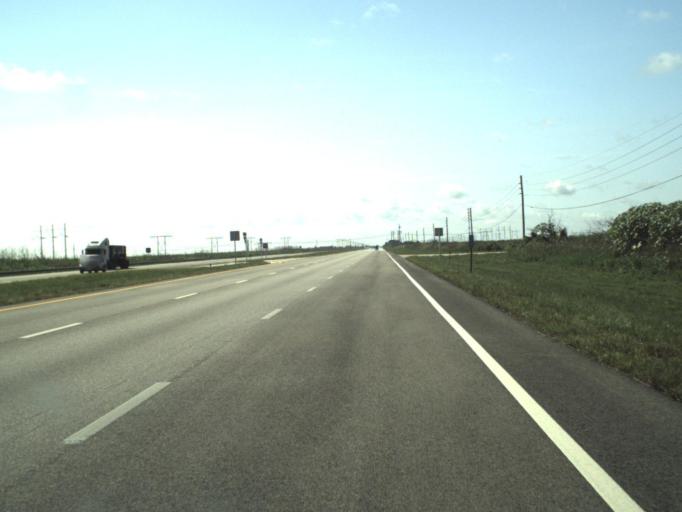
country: US
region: Florida
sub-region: Broward County
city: Coral Springs
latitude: 26.3546
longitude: -80.5533
